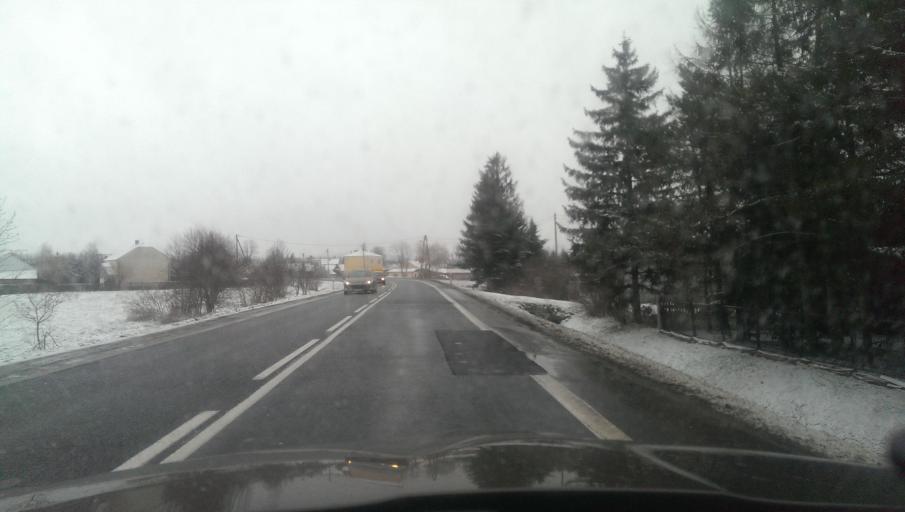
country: PL
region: Subcarpathian Voivodeship
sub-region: Powiat sanocki
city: Zarszyn
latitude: 49.5820
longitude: 22.0021
